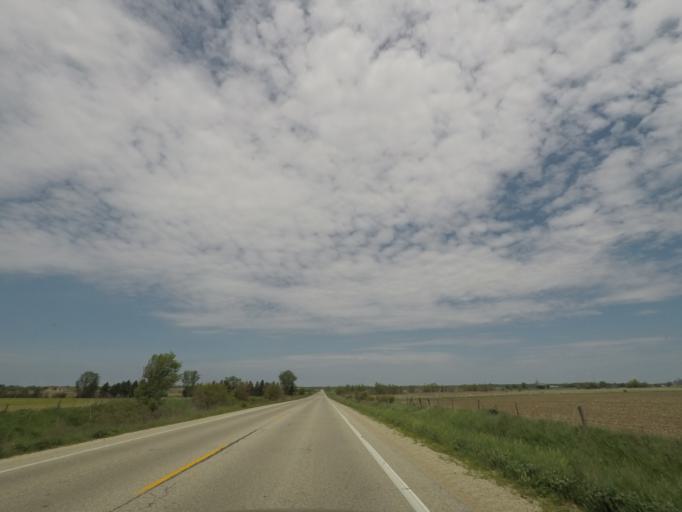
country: US
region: Wisconsin
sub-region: Rock County
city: Evansville
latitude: 42.7422
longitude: -89.2989
